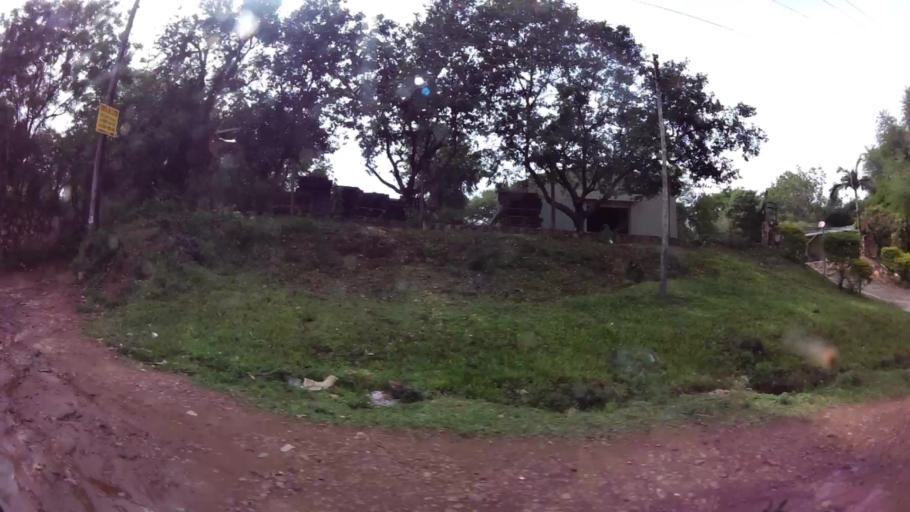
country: PY
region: Central
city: Limpio
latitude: -25.1531
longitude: -57.4621
